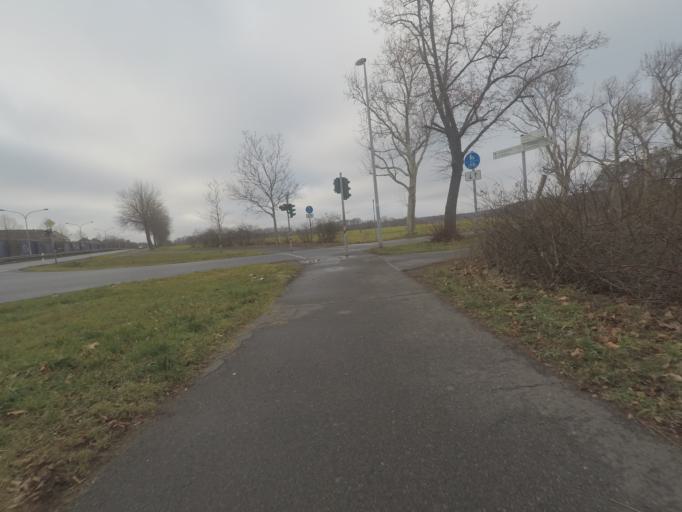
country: DE
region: Berlin
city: Lichtenrade
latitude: 52.3674
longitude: 13.4131
